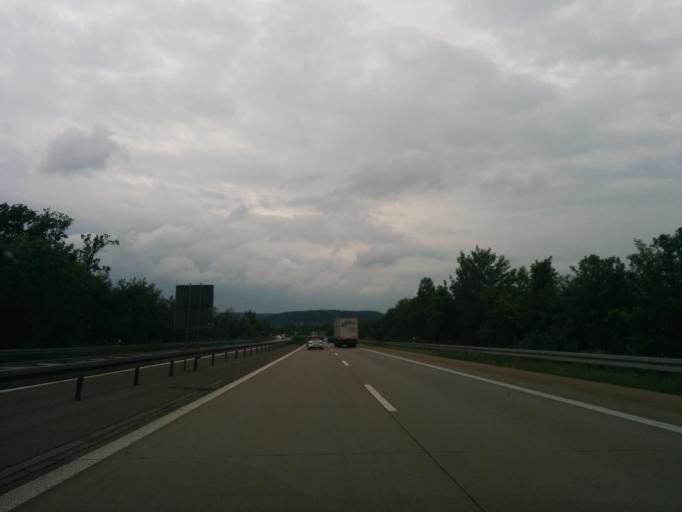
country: DE
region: Bavaria
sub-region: Regierungsbezirk Mittelfranken
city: Schopfloch
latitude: 49.1421
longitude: 10.2634
